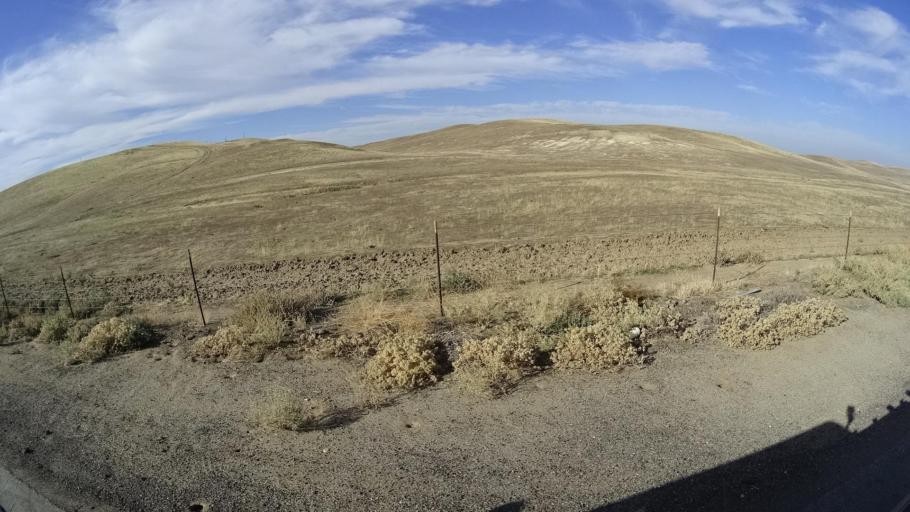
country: US
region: California
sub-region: Kern County
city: Oildale
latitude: 35.6204
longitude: -118.9868
